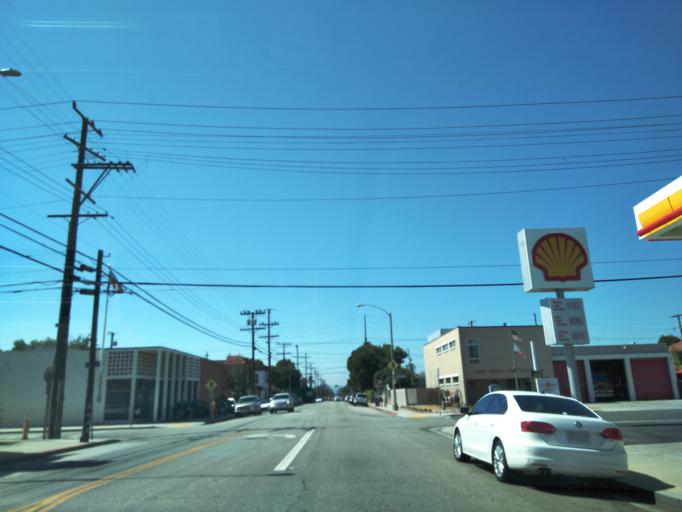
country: US
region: California
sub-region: Los Angeles County
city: Signal Hill
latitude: 33.7717
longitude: -118.1500
